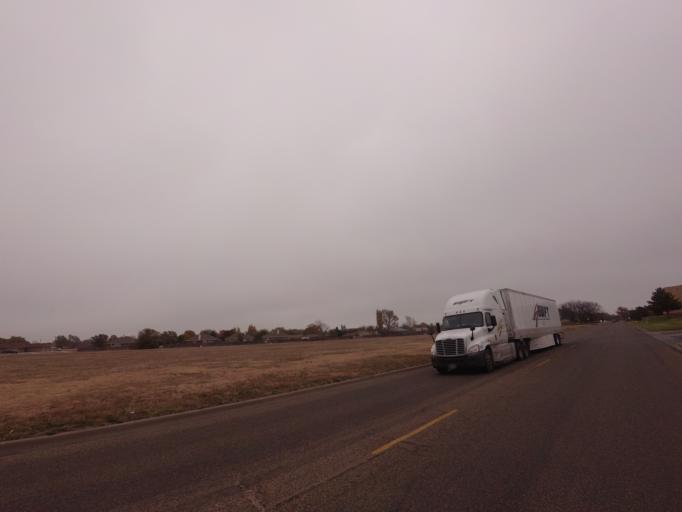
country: US
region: New Mexico
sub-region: Curry County
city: Clovis
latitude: 34.4253
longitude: -103.1915
